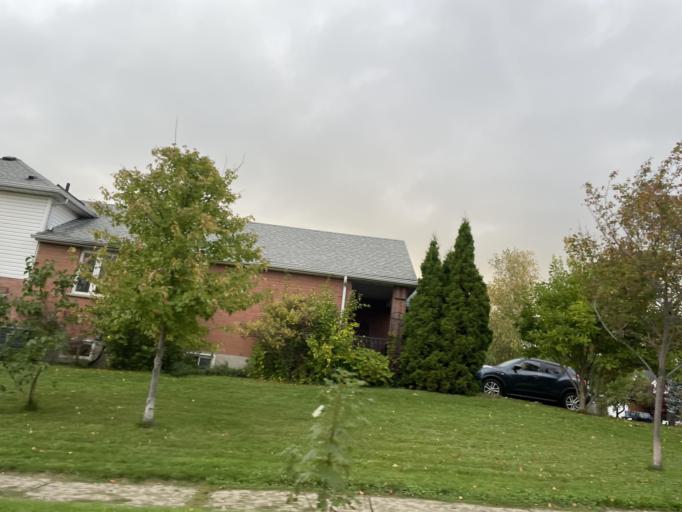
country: CA
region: Ontario
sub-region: Wellington County
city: Guelph
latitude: 43.5040
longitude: -80.2451
